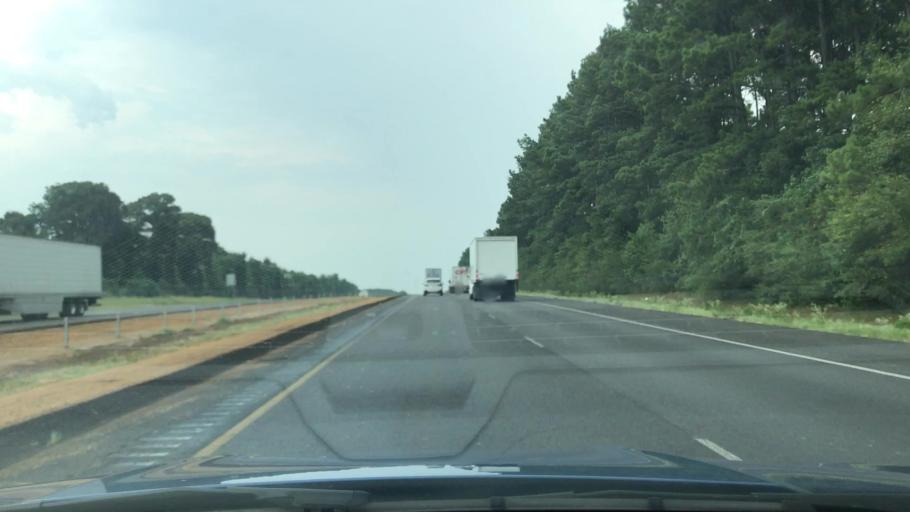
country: US
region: Texas
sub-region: Harrison County
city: Marshall
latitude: 32.4953
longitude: -94.2558
